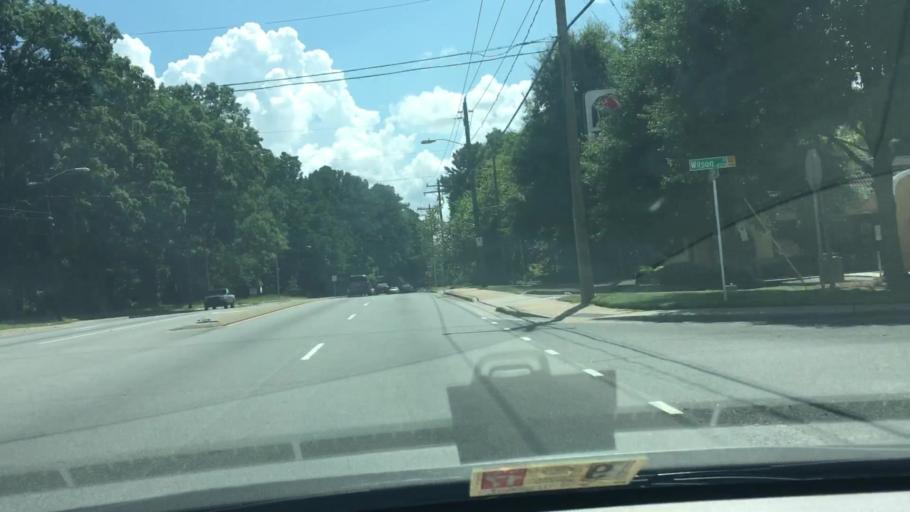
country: US
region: North Carolina
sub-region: Mecklenburg County
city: Charlotte
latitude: 35.2754
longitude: -80.7936
